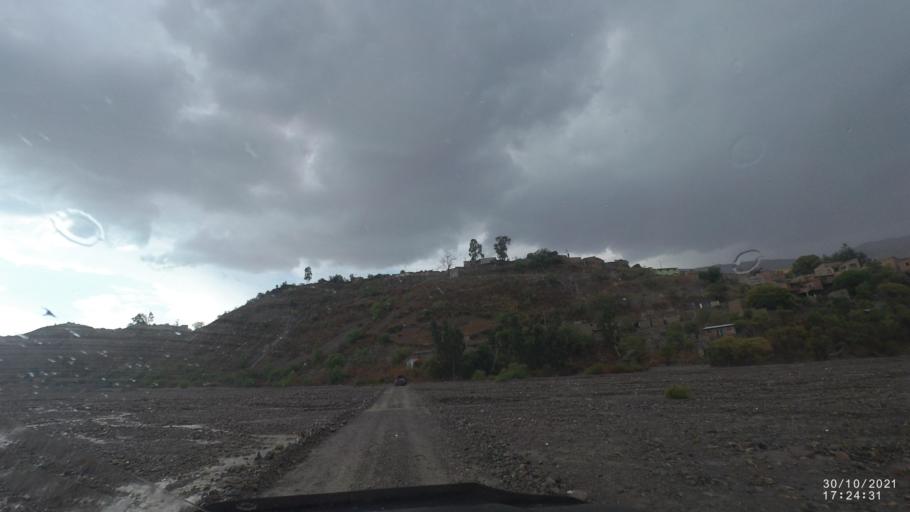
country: BO
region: Cochabamba
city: Colchani
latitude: -17.5182
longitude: -66.6223
